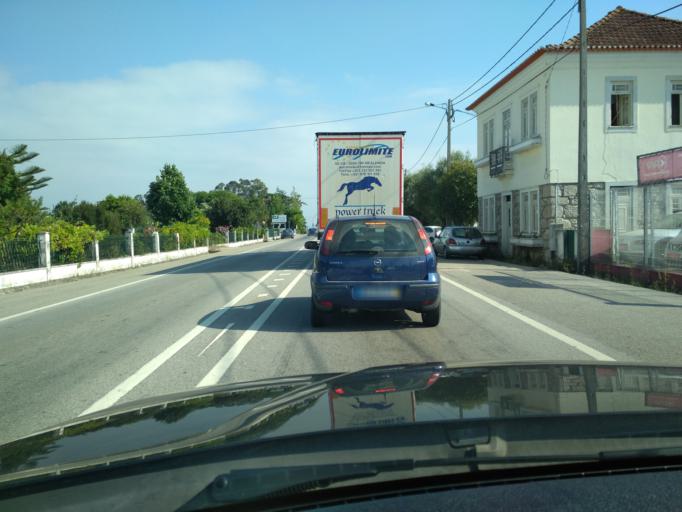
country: PT
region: Aveiro
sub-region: Mealhada
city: Pampilhosa do Botao
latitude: 40.3066
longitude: -8.4487
